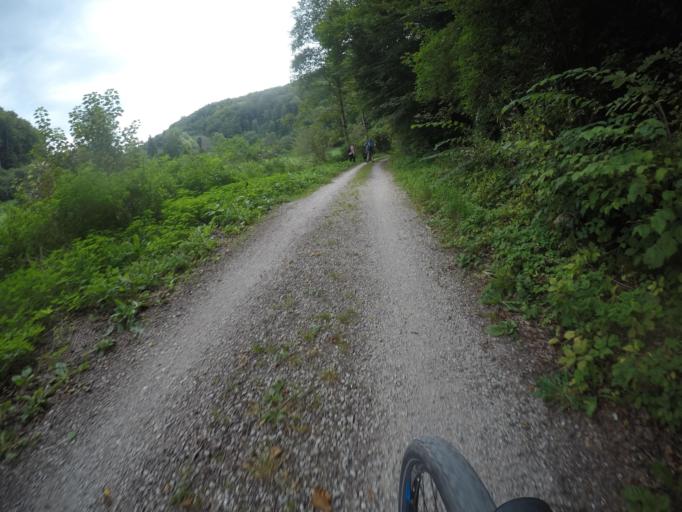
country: DE
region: Baden-Wuerttemberg
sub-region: Tuebingen Region
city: Bad Urach
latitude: 48.4509
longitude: 9.4375
